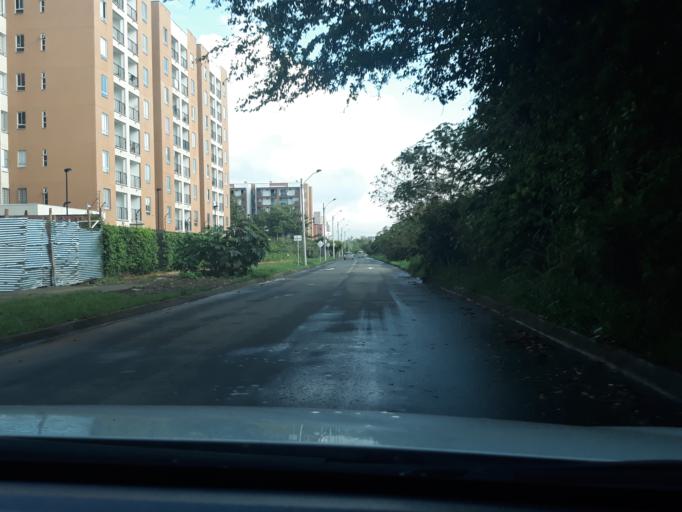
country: CO
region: Valle del Cauca
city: Cali
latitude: 3.3546
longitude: -76.5164
